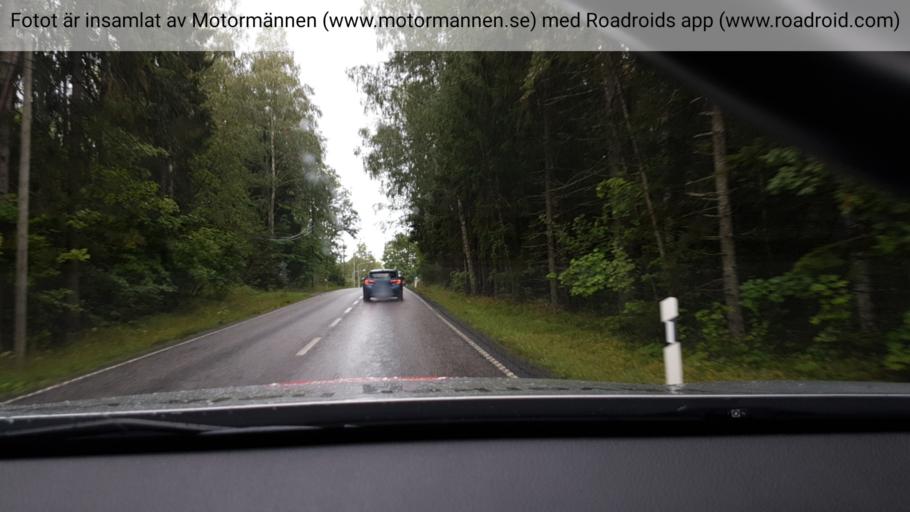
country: SE
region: Stockholm
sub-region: Norrtalje Kommun
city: Hallstavik
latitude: 59.9718
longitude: 18.6026
